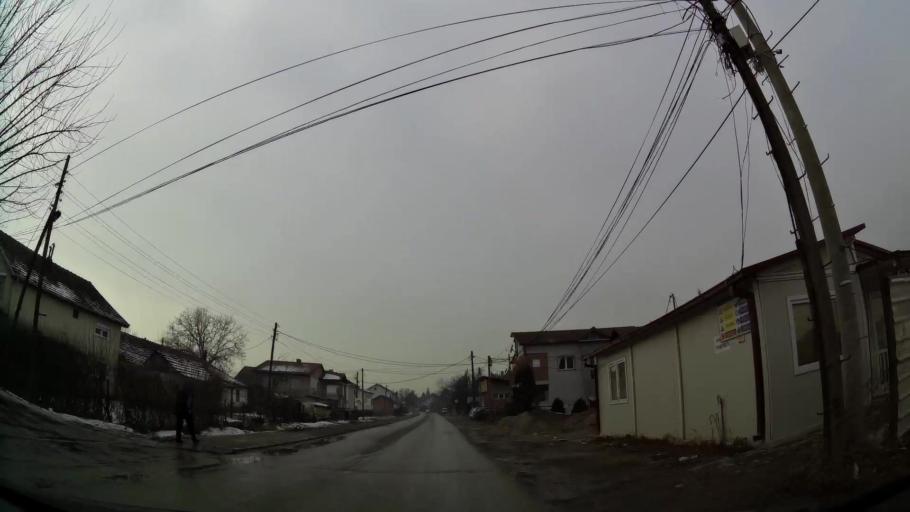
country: MK
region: Ilinden
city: Ilinden
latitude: 41.9966
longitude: 21.5800
